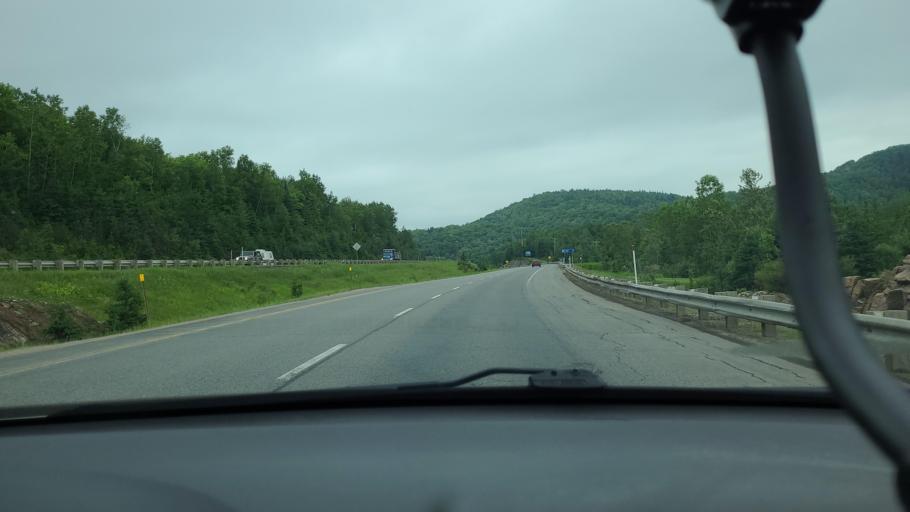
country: CA
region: Quebec
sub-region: Laurentides
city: Mont-Tremblant
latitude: 46.1409
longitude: -74.6492
